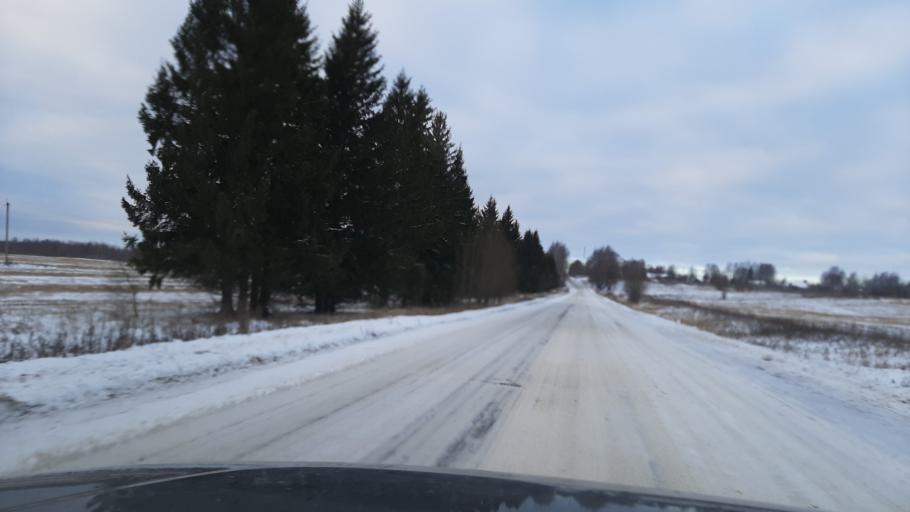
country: RU
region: Kostroma
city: Kosmynino
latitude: 57.4819
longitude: 40.7803
